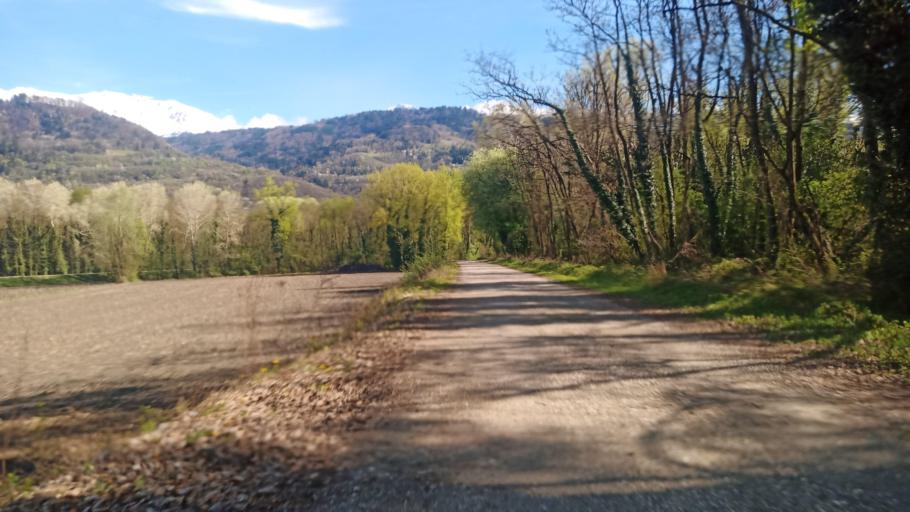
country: FR
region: Rhone-Alpes
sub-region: Departement de l'Isere
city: Froges
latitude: 45.2848
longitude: 5.9177
